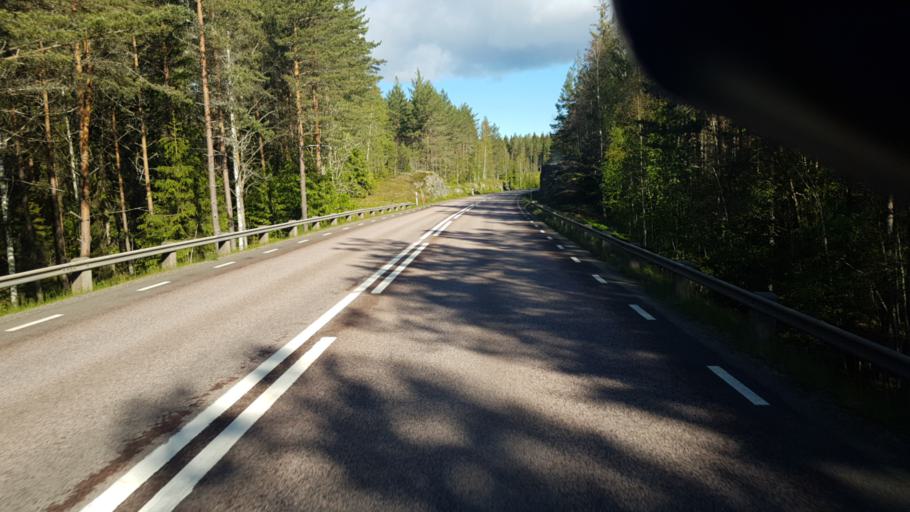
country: SE
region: Vaermland
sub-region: Arvika Kommun
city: Arvika
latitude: 59.5883
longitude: 12.6516
